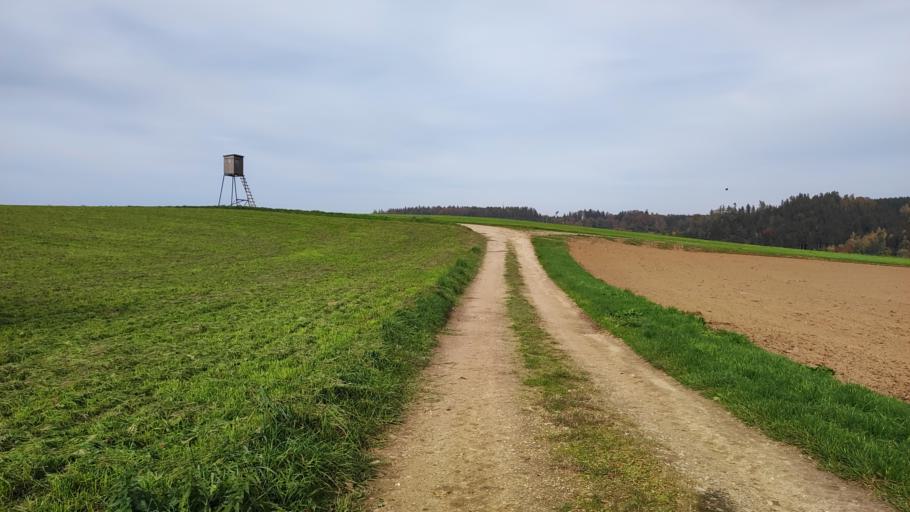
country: DE
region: Bavaria
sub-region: Swabia
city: Ziemetshausen
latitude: 48.2788
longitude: 10.5634
